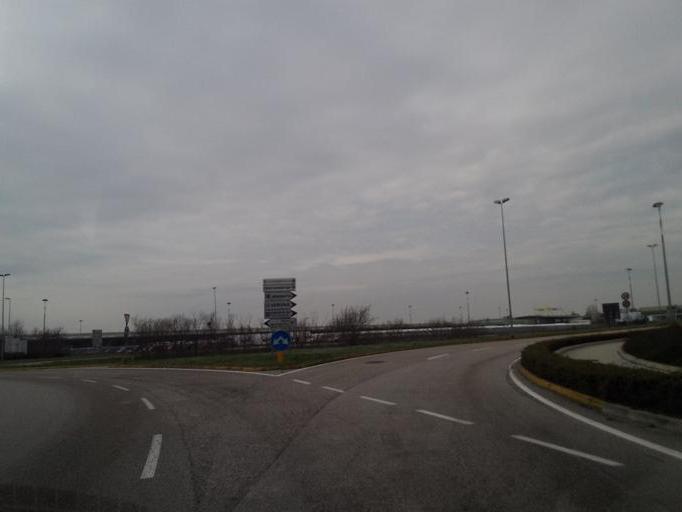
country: IT
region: Veneto
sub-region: Provincia di Verona
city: Dossobuono
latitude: 45.4109
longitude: 10.9280
